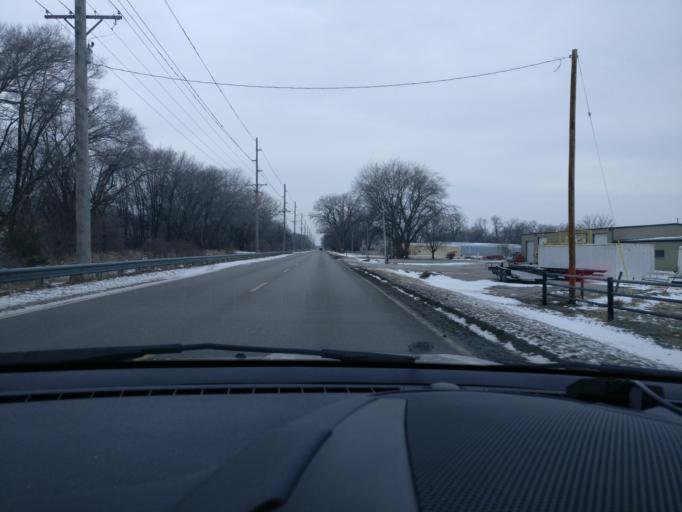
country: US
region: Nebraska
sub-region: Dodge County
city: Fremont
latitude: 41.4399
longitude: -96.5277
